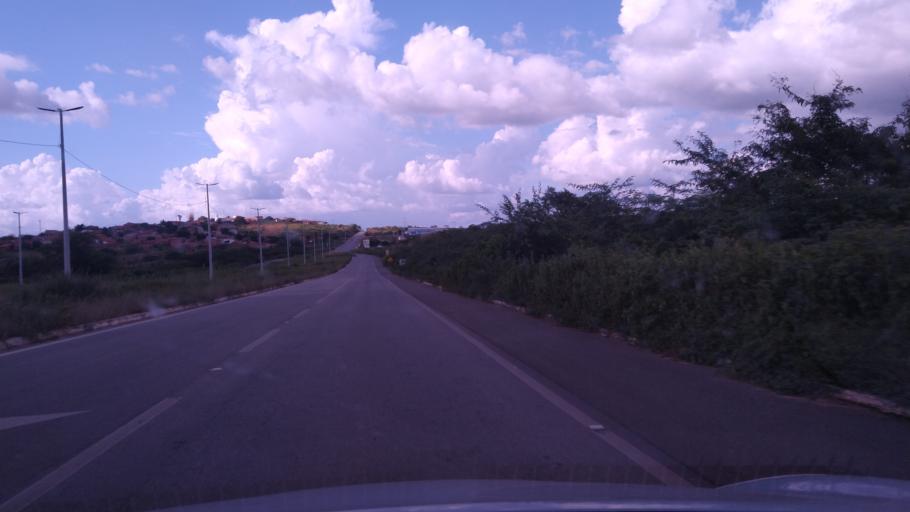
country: BR
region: Ceara
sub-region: Caninde
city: Caninde
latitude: -4.3785
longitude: -39.3087
